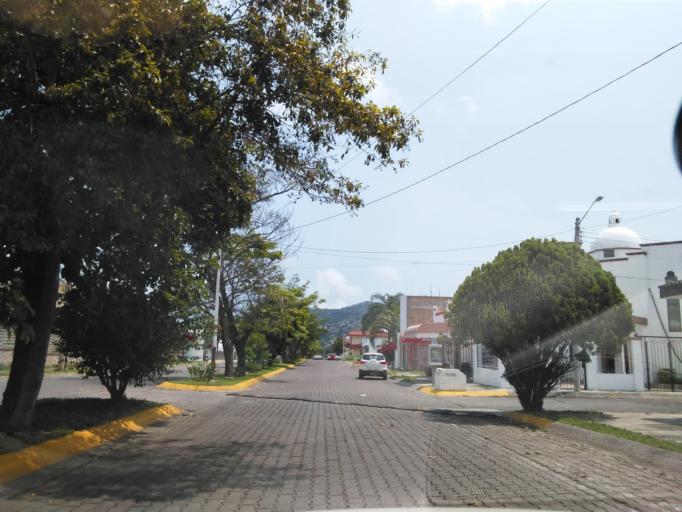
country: MX
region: Nayarit
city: Tepic
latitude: 21.5175
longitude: -104.9227
